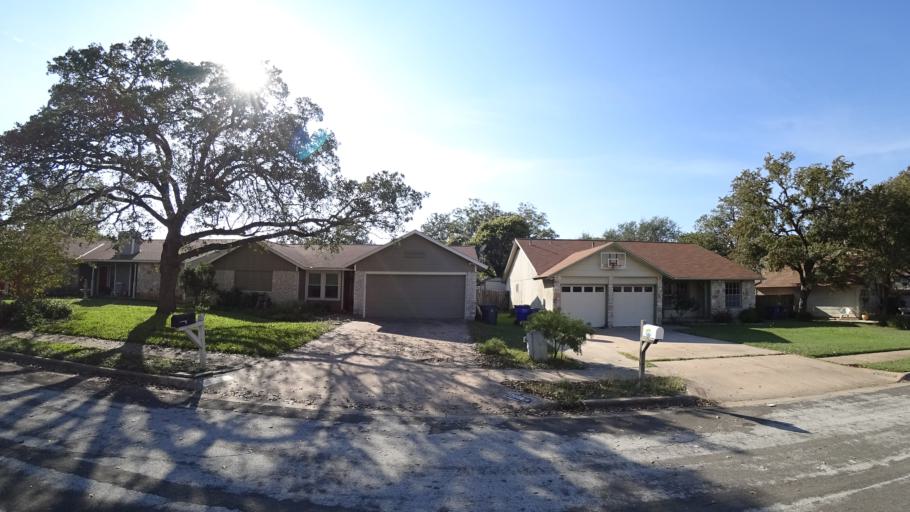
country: US
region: Texas
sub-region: Williamson County
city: Anderson Mill
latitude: 30.4576
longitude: -97.8154
